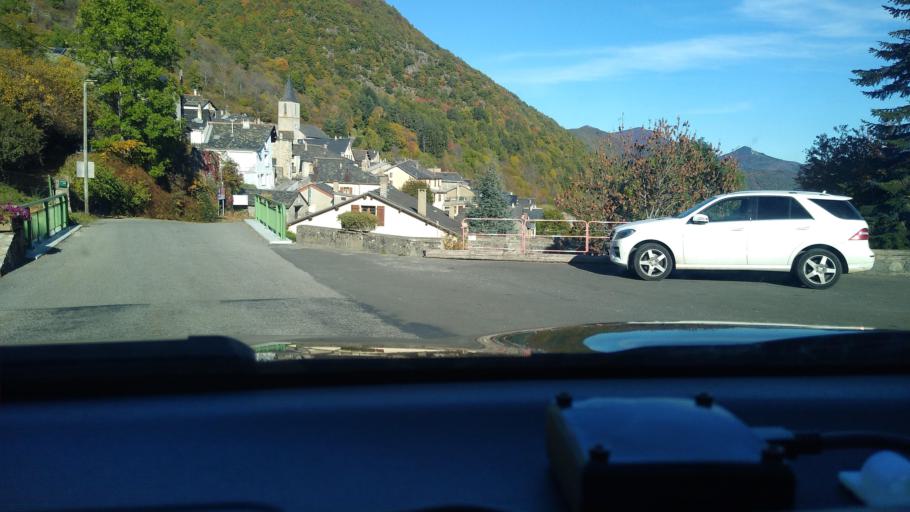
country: FR
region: Languedoc-Roussillon
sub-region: Departement de l'Aude
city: Quillan
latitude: 42.7294
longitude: 2.0548
